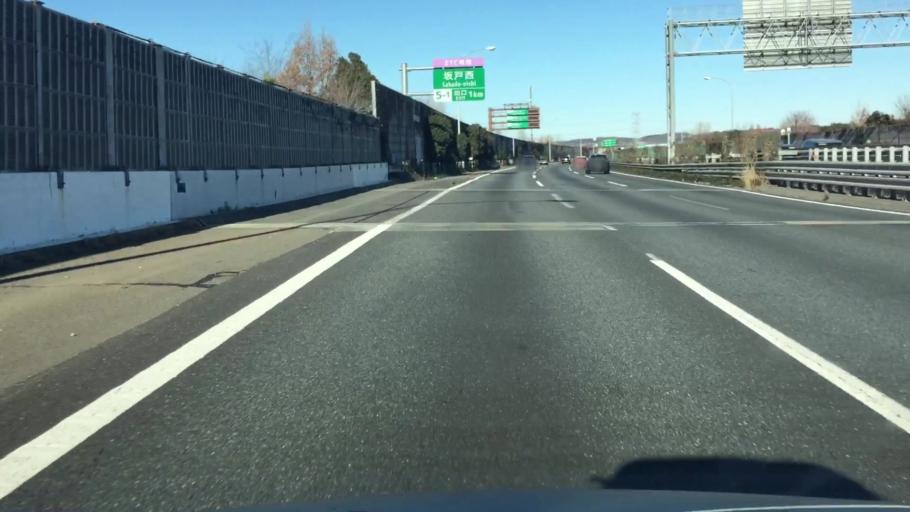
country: JP
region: Saitama
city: Sakado
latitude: 35.9553
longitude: 139.3843
